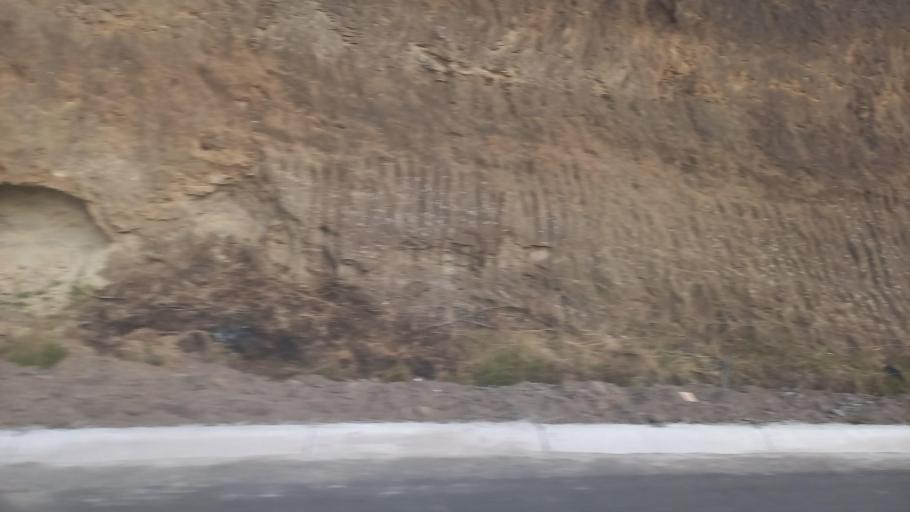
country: EC
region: Pichincha
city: Cayambe
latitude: 0.1252
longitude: -78.0740
